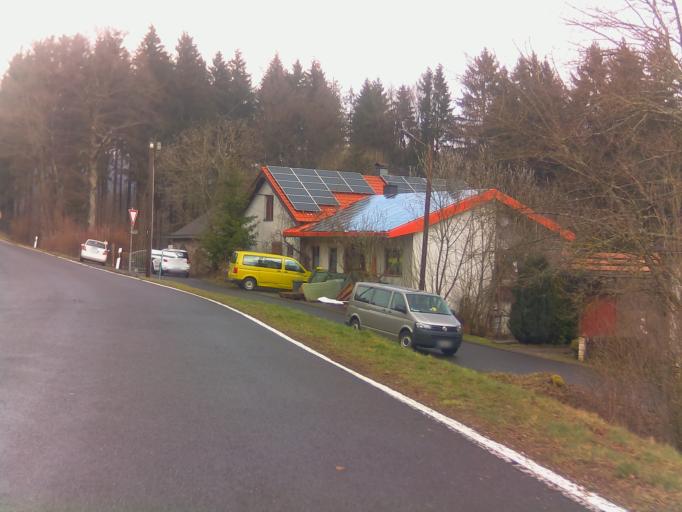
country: DE
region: Rheinland-Pfalz
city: Borfink
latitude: 49.6906
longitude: 7.0805
